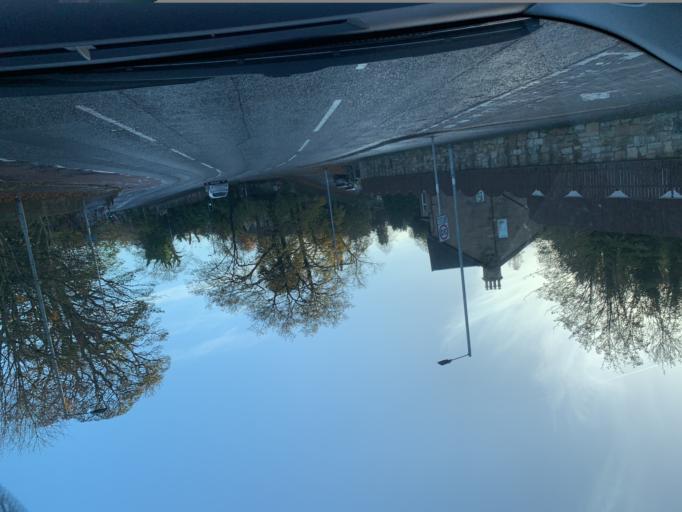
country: GB
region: Scotland
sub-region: East Renfrewshire
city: Giffnock
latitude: 55.8172
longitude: -4.3025
